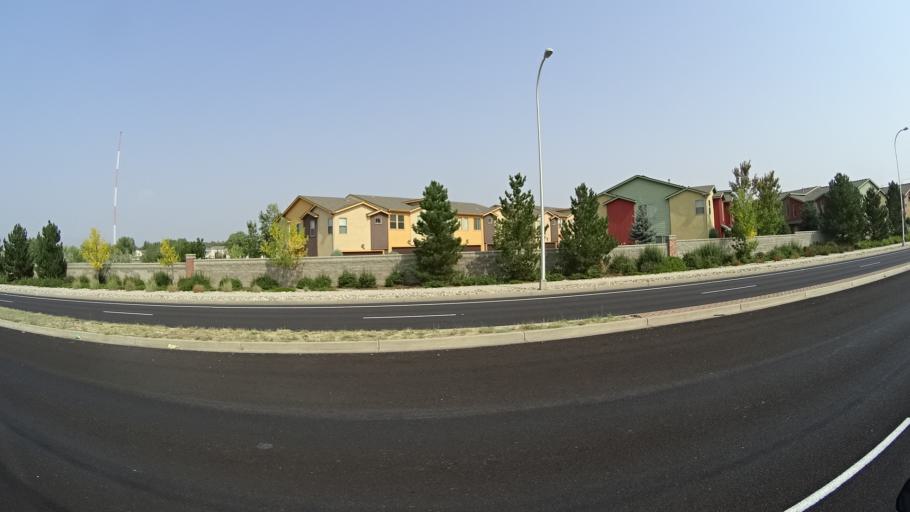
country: US
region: Colorado
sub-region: El Paso County
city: Cimarron Hills
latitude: 38.8253
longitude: -104.7404
